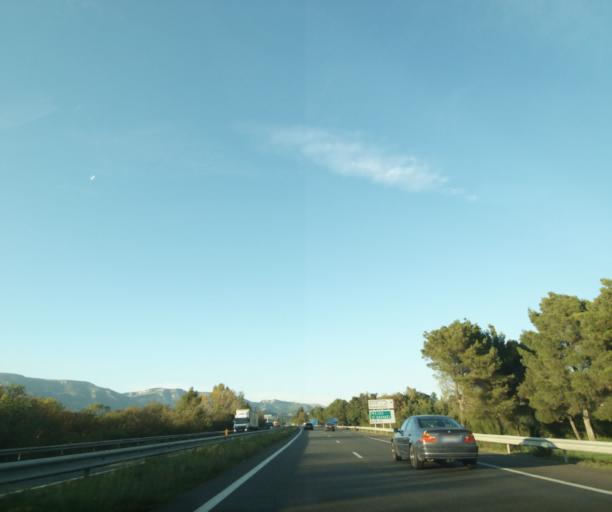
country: FR
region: Provence-Alpes-Cote d'Azur
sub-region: Departement des Bouches-du-Rhone
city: Aubagne
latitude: 43.3081
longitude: 5.5921
